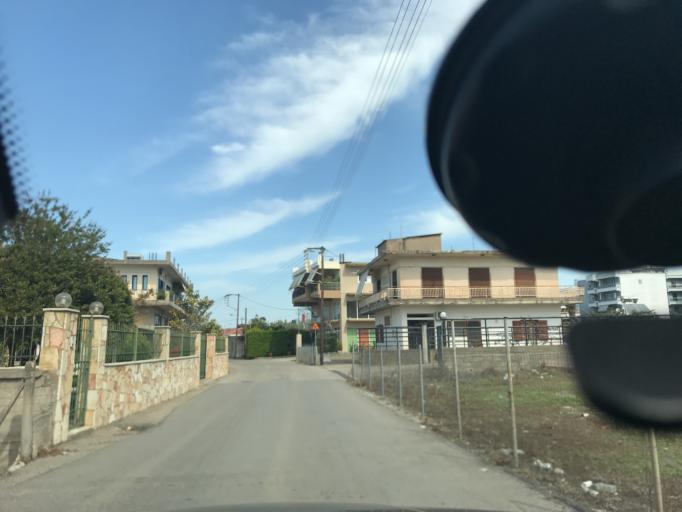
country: GR
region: West Greece
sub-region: Nomos Ileias
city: Pyrgos
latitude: 37.6786
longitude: 21.4391
